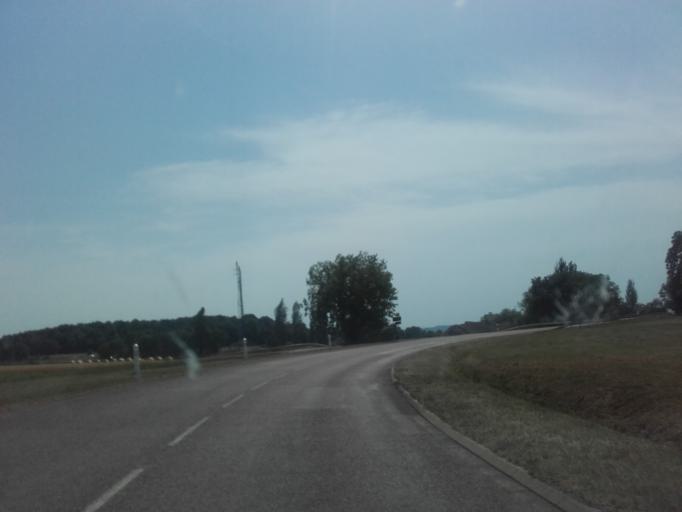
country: FR
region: Bourgogne
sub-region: Departement de Saone-et-Loire
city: Demigny
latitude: 46.9225
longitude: 4.8221
